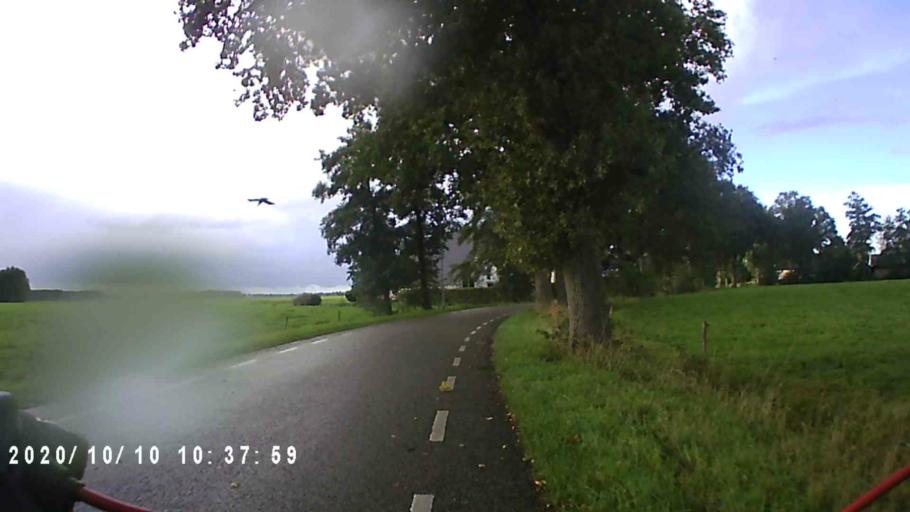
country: NL
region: Groningen
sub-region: Gemeente Grootegast
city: Grootegast
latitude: 53.1819
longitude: 6.2983
